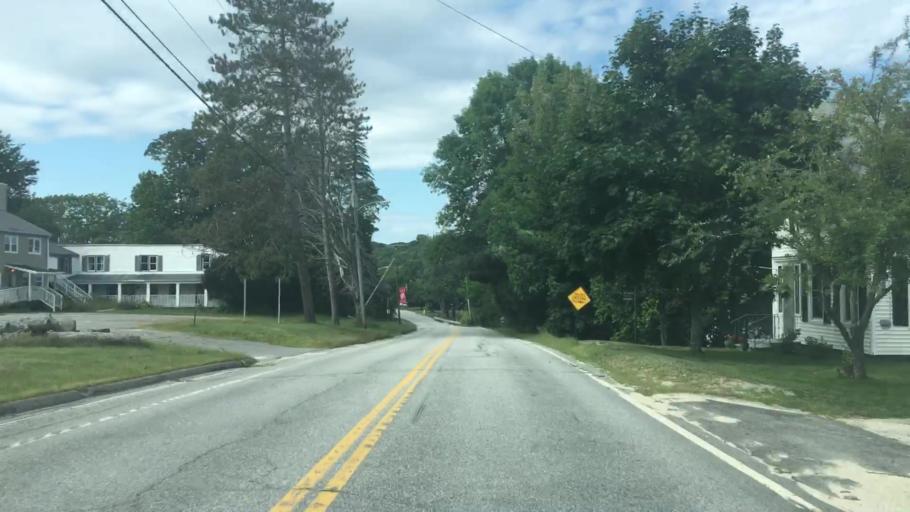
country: US
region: Maine
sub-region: Cumberland County
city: Raymond
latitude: 44.0081
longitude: -70.5228
